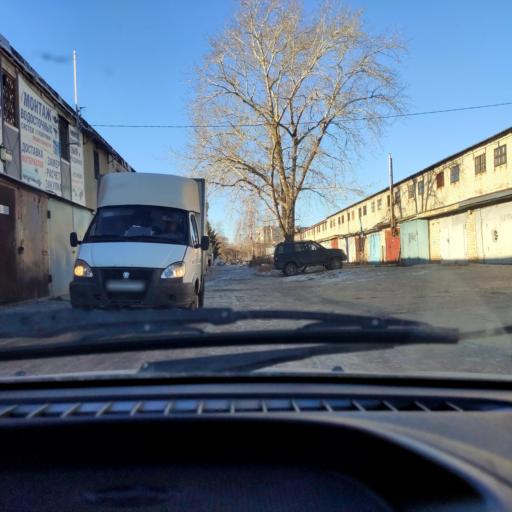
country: RU
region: Samara
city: Tol'yatti
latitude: 53.5136
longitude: 49.4341
